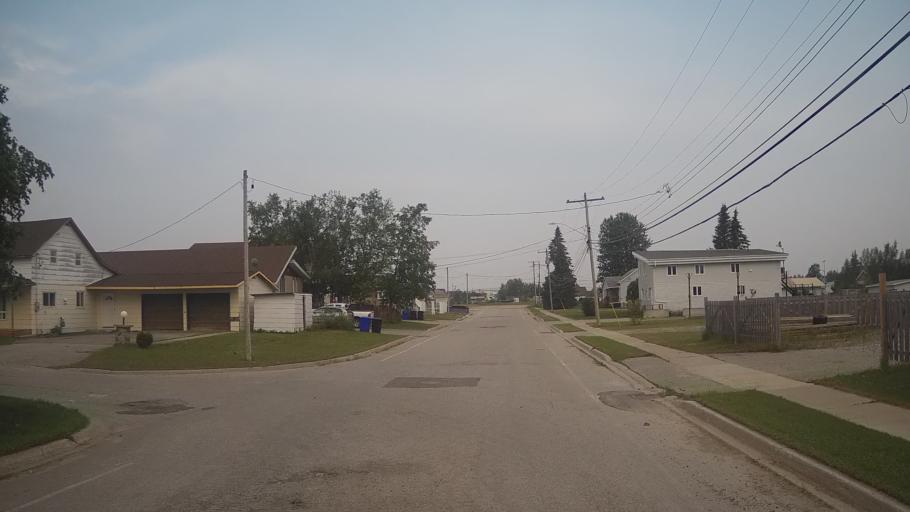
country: CA
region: Ontario
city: Hearst
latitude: 49.6895
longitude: -83.6514
